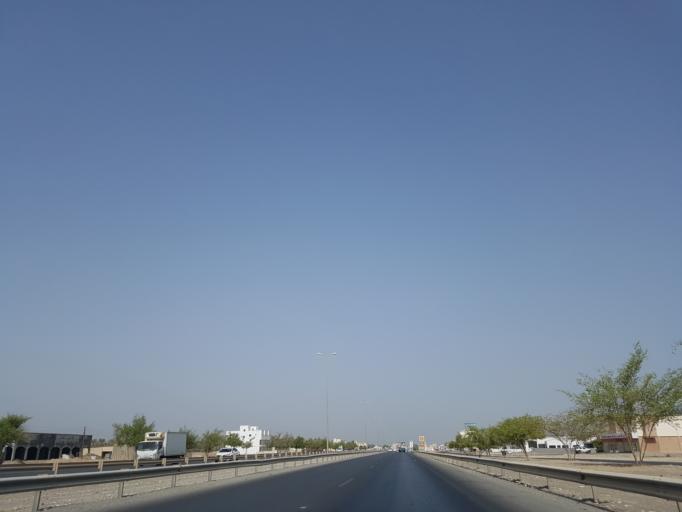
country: OM
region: Al Batinah
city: As Suwayq
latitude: 23.7421
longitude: 57.6340
